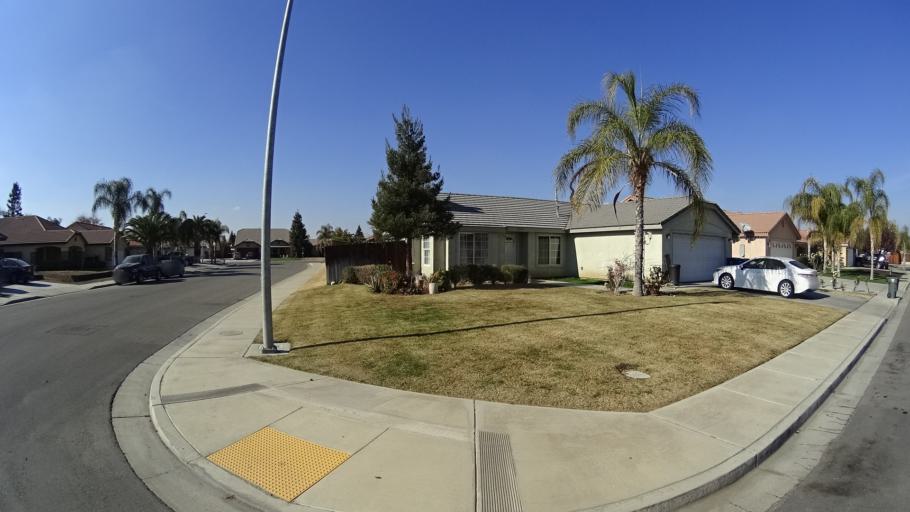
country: US
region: California
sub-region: Kern County
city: Greenfield
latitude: 35.2910
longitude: -119.0417
